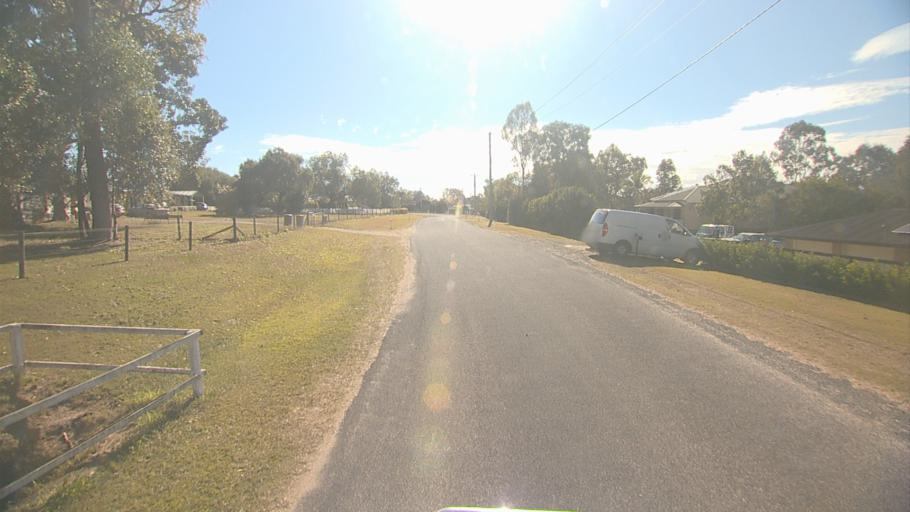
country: AU
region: Queensland
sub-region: Logan
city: Chambers Flat
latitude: -27.7738
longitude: 153.0805
